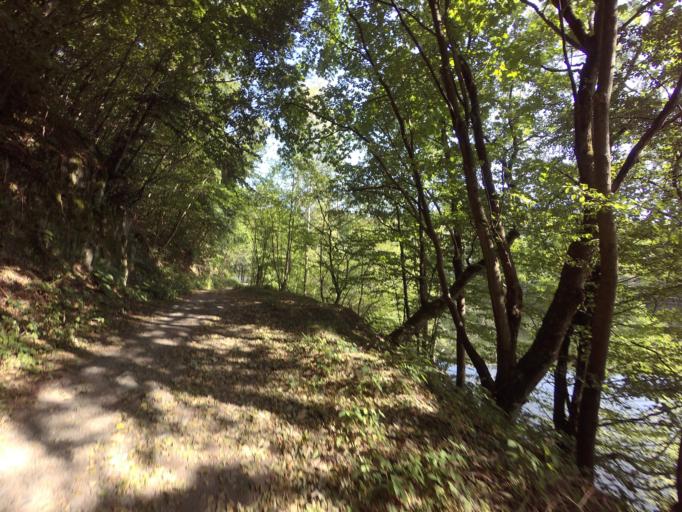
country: DE
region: North Rhine-Westphalia
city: Heimbach
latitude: 50.6014
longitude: 6.4104
